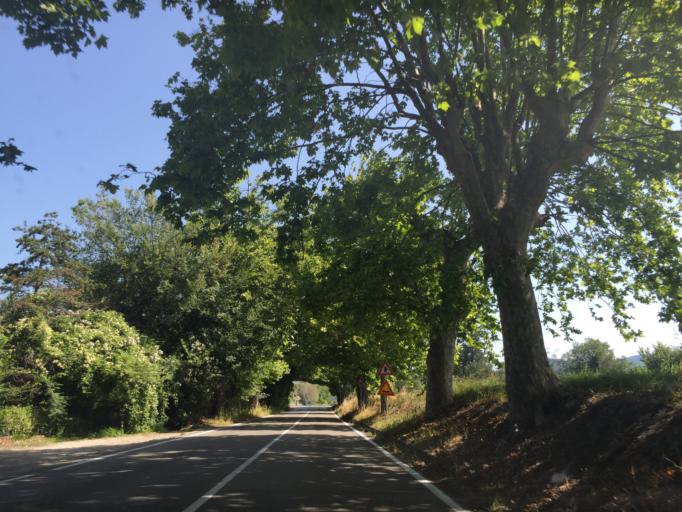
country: IT
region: Tuscany
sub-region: Province of Pisa
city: Gello
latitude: 43.7358
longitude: 10.4234
